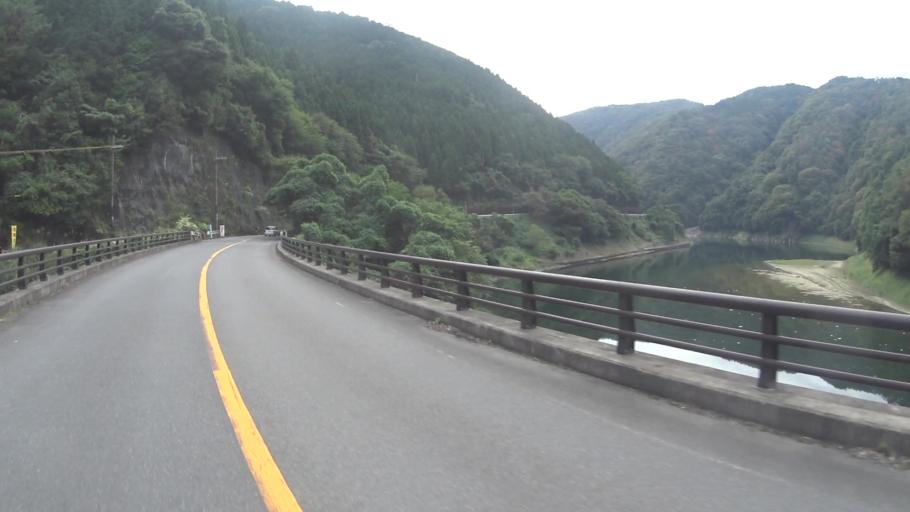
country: JP
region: Kyoto
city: Uji
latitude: 34.8832
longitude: 135.8597
